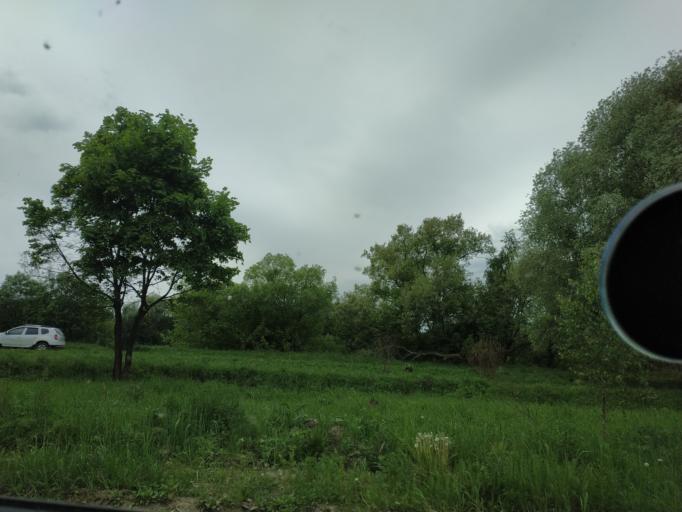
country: RU
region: Moskovskaya
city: Ostrovtsy
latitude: 55.5600
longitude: 38.0293
